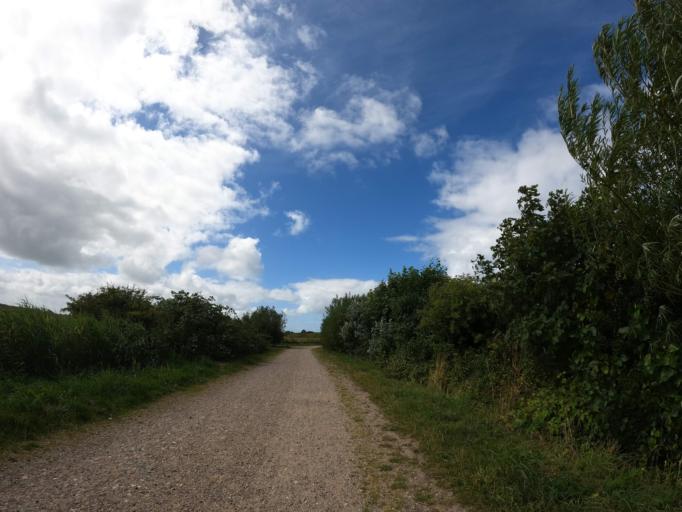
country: DE
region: Schleswig-Holstein
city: Tinnum
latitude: 54.8955
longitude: 8.3242
